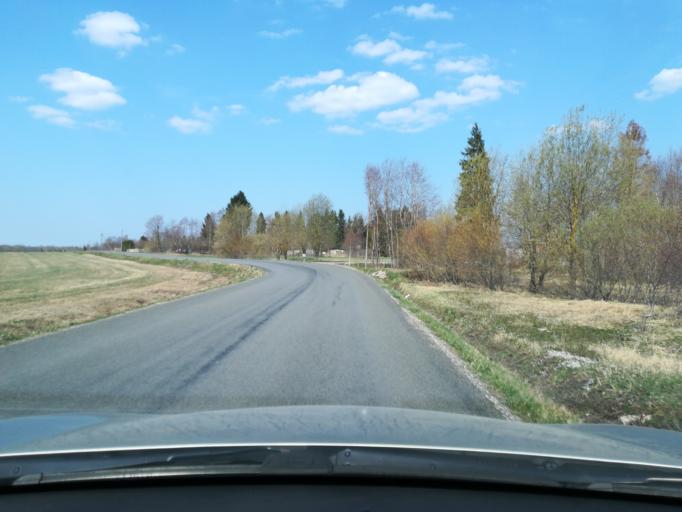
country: EE
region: Harju
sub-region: Saue linn
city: Saue
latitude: 59.3590
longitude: 24.5641
